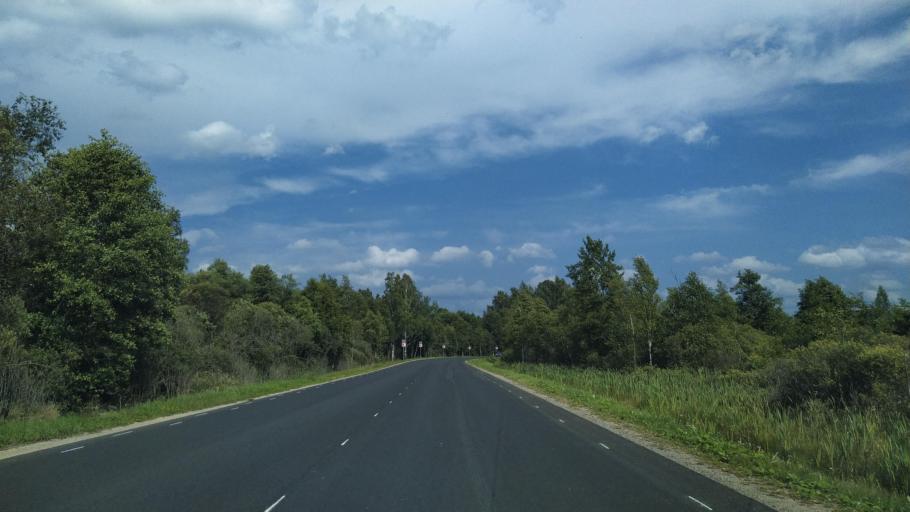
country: RU
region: Pskov
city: Vybor
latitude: 57.7404
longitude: 29.0165
